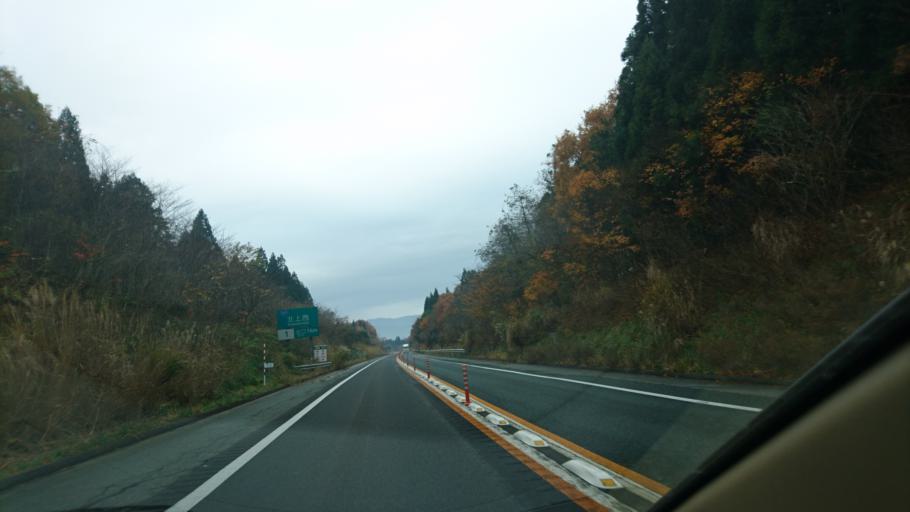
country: JP
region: Iwate
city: Kitakami
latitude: 39.2853
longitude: 140.9958
